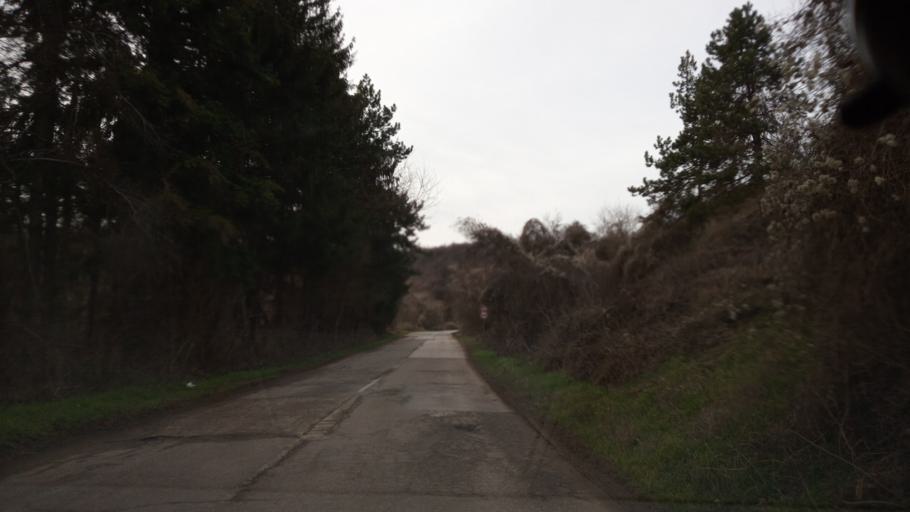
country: BG
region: Pleven
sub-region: Obshtina Belene
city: Belene
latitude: 43.5970
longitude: 24.9925
